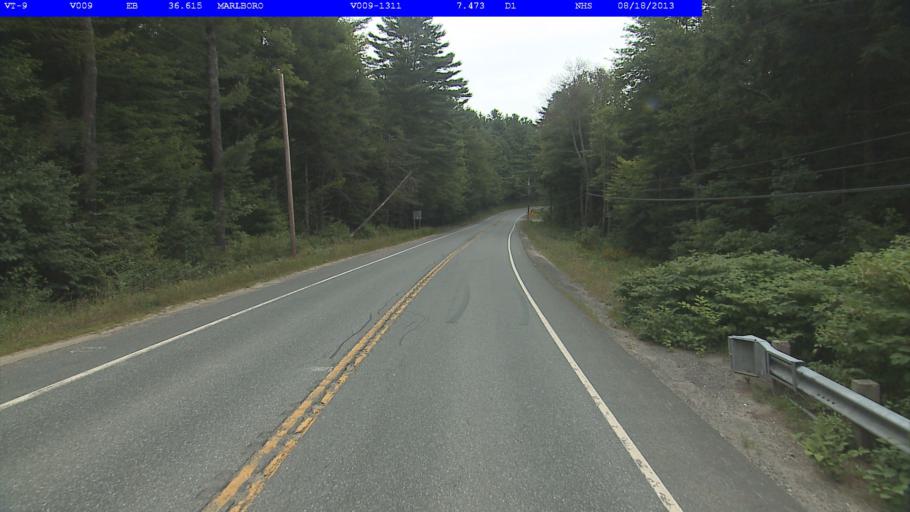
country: US
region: Vermont
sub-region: Windham County
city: West Brattleboro
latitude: 42.8780
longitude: -72.6914
